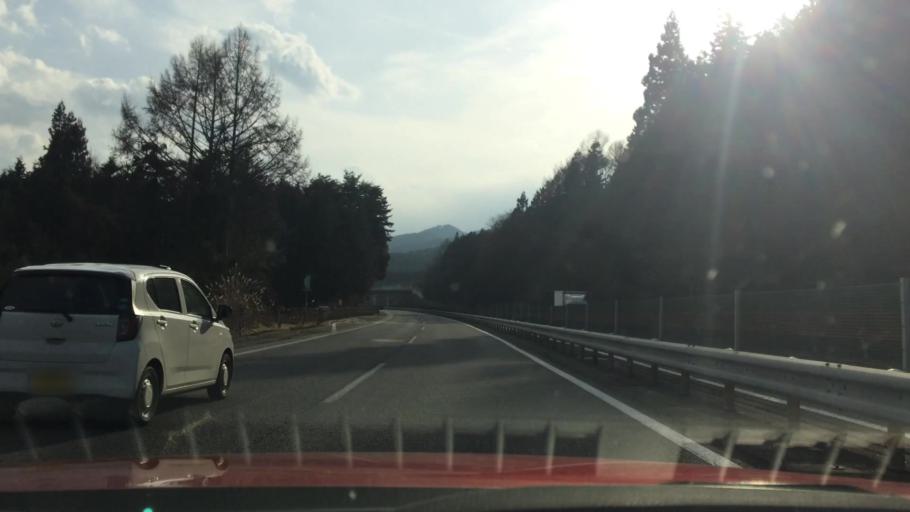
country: JP
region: Nagano
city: Ina
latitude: 35.8199
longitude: 137.9265
